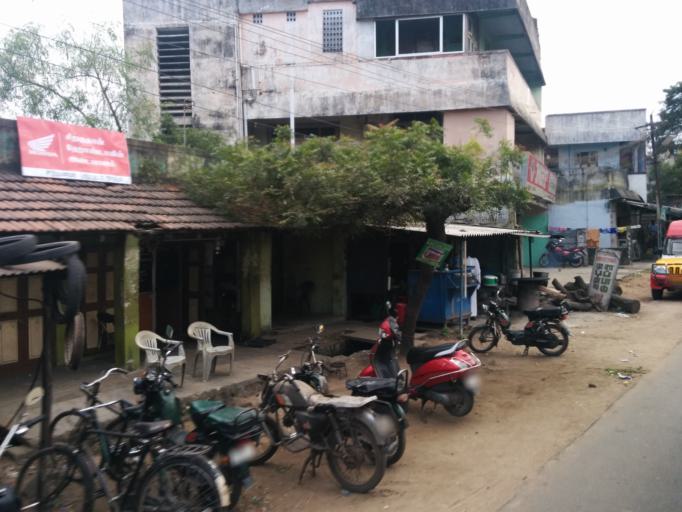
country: IN
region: Tamil Nadu
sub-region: Kancheepuram
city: Madurantakam
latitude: 12.5128
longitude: 79.8866
